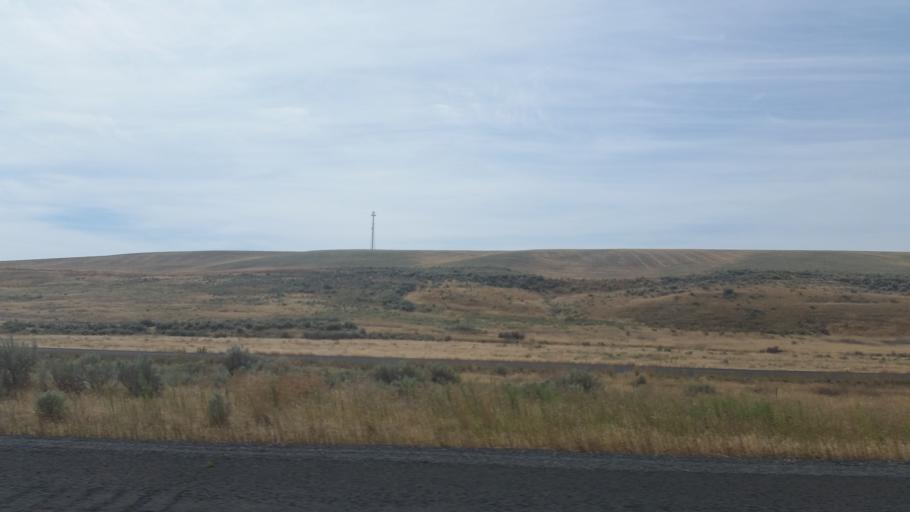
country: US
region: Washington
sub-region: Adams County
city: Ritzville
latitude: 47.1111
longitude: -118.5651
